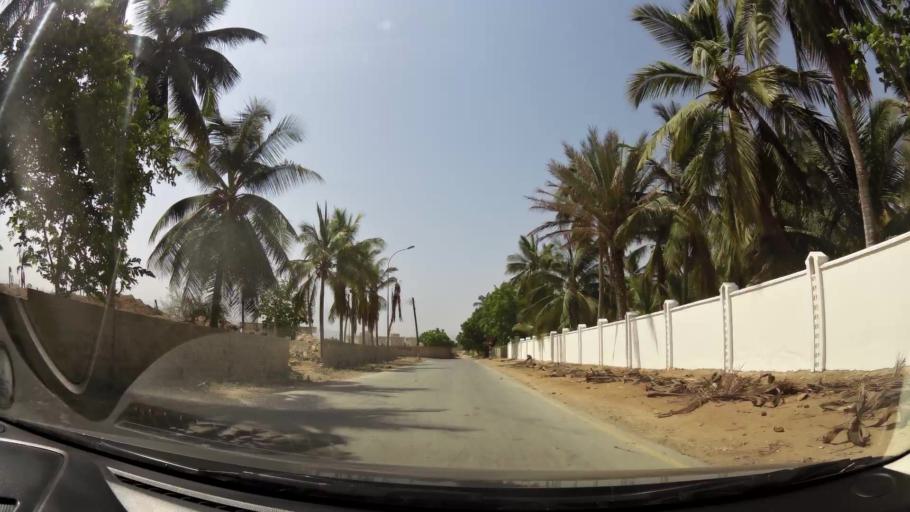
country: OM
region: Zufar
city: Salalah
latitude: 17.0195
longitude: 54.0729
